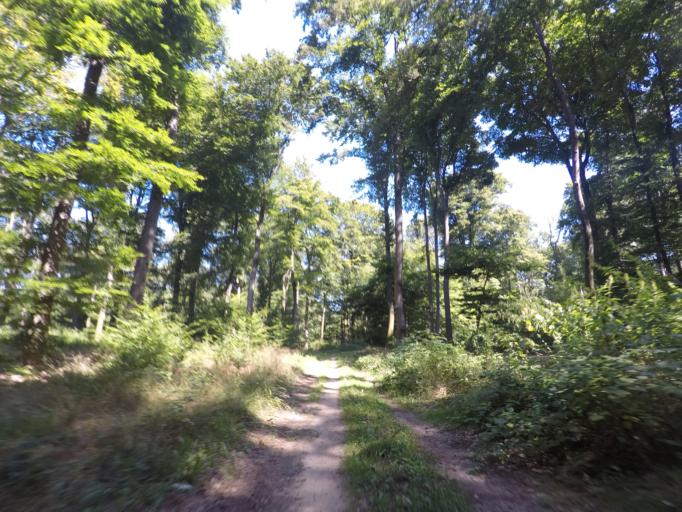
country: LU
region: Luxembourg
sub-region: Canton de Capellen
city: Kopstal
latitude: 49.6444
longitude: 6.0657
